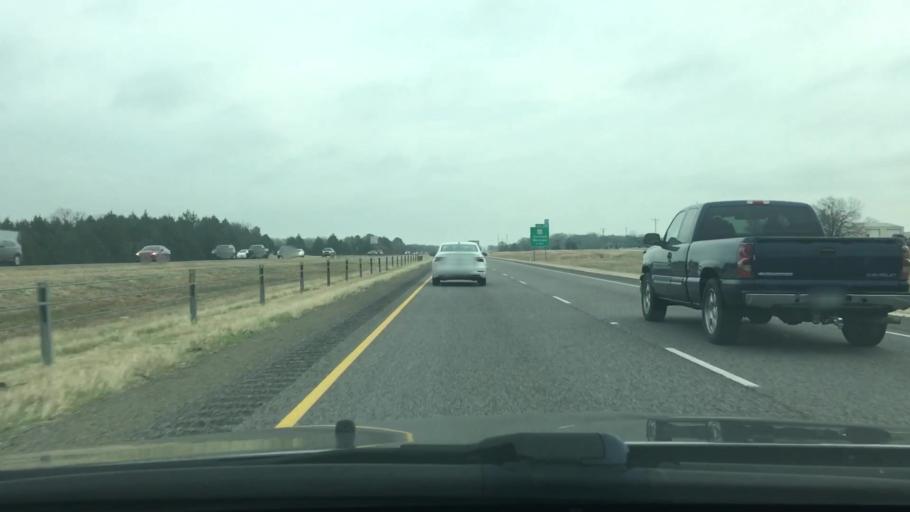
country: US
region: Texas
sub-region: Freestone County
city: Fairfield
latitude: 31.7427
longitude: -96.1927
